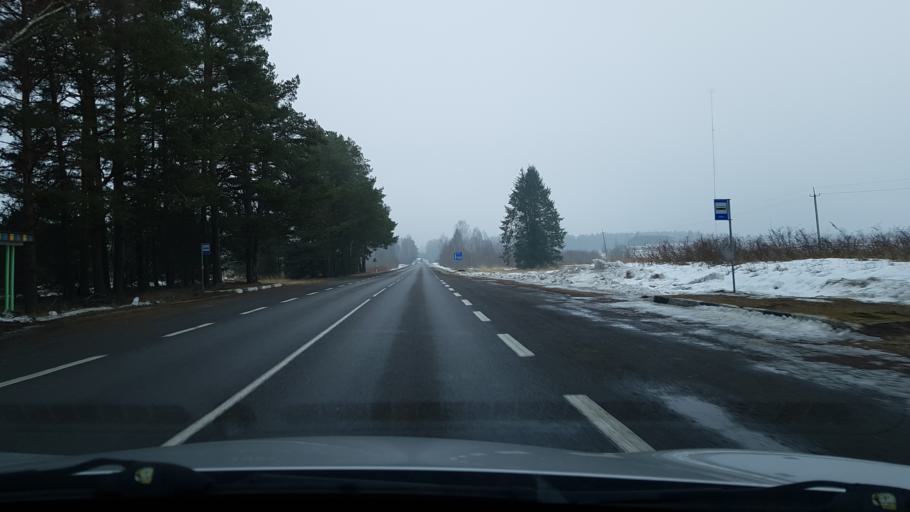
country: EE
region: Valgamaa
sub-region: Torva linn
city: Torva
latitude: 58.0890
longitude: 26.0231
